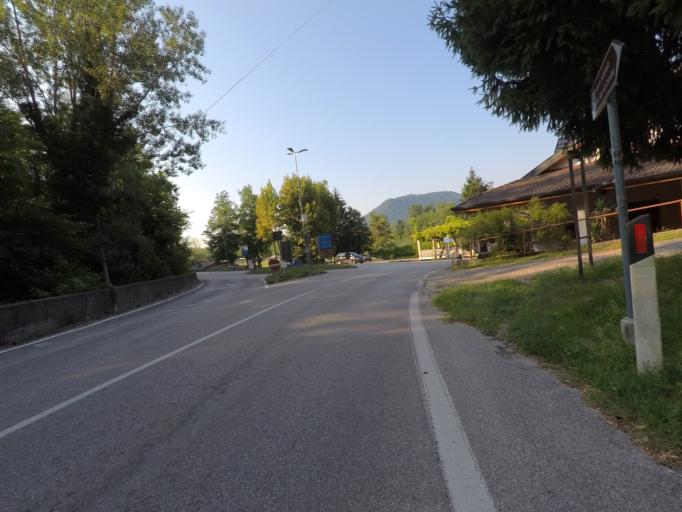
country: IT
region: Friuli Venezia Giulia
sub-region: Provincia di Udine
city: Forgaria nel Friuli
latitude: 46.2234
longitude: 13.0088
